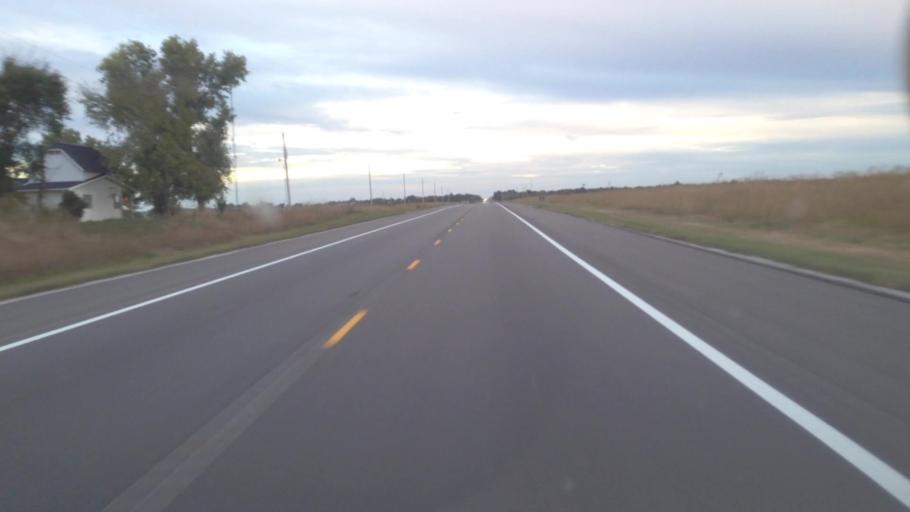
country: US
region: Kansas
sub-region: Anderson County
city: Garnett
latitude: 38.4252
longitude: -95.2487
